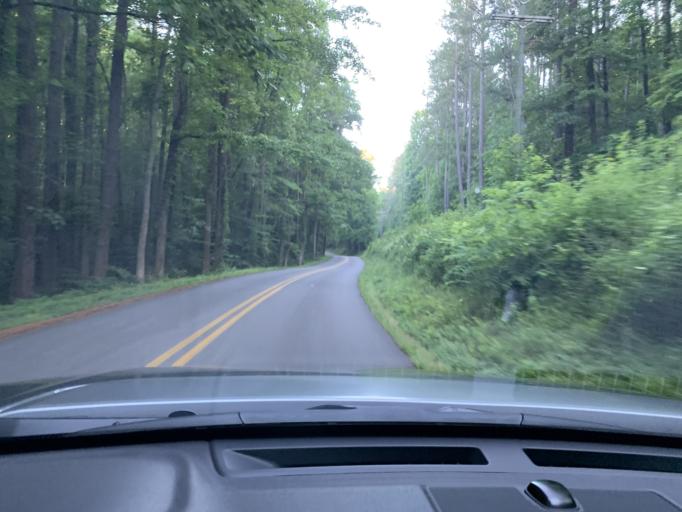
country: US
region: Georgia
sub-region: Bartow County
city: Rydal
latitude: 34.2307
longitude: -84.6606
